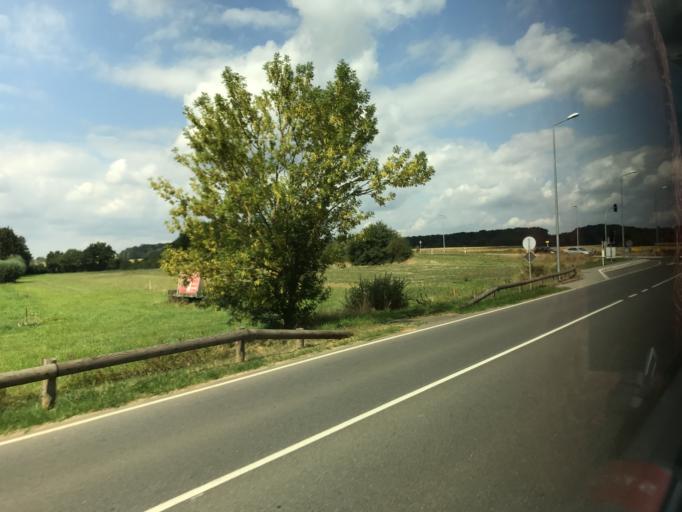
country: LU
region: Luxembourg
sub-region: Canton d'Esch-sur-Alzette
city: Frisange
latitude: 49.5330
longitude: 6.1800
